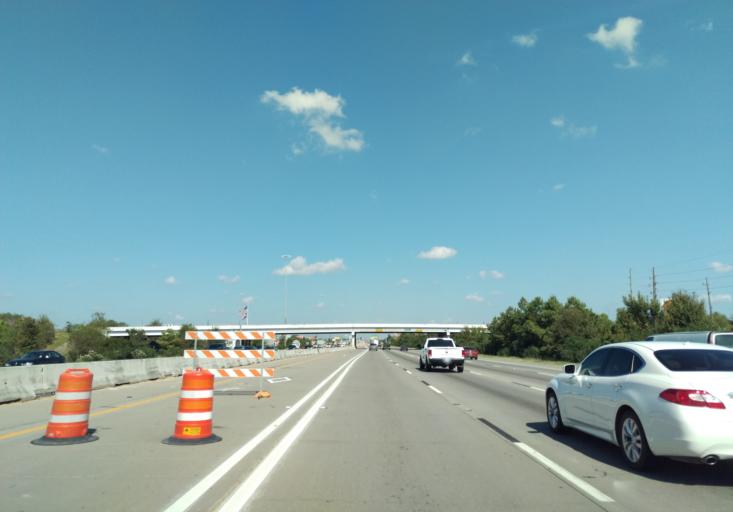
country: US
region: Texas
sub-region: Harris County
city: Spring
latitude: 30.0648
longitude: -95.4340
